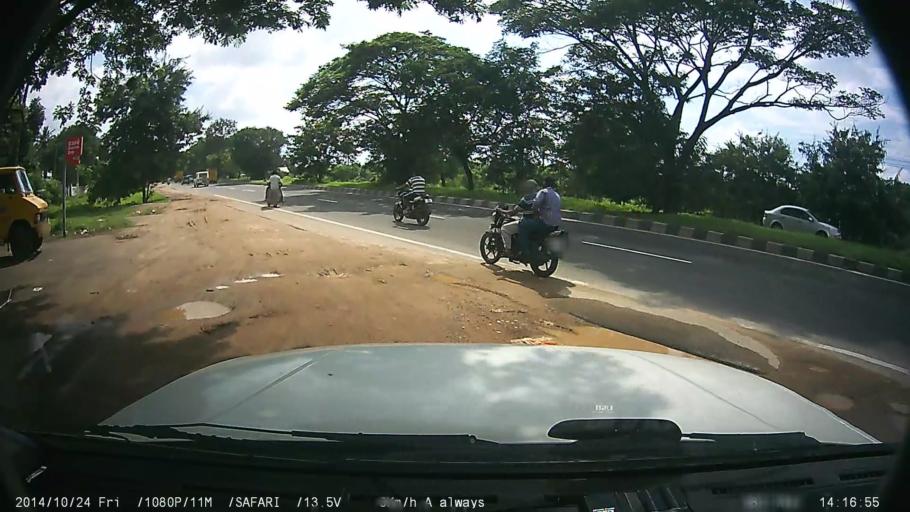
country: IN
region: Tamil Nadu
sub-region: Kancheepuram
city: Singapperumalkovil
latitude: 12.7747
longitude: 80.0097
